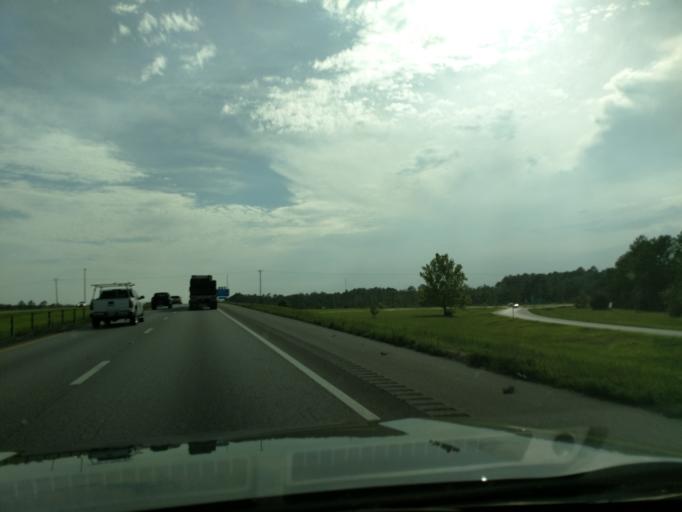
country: US
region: Alabama
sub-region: Mobile County
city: Grand Bay
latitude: 30.4677
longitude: -88.4167
